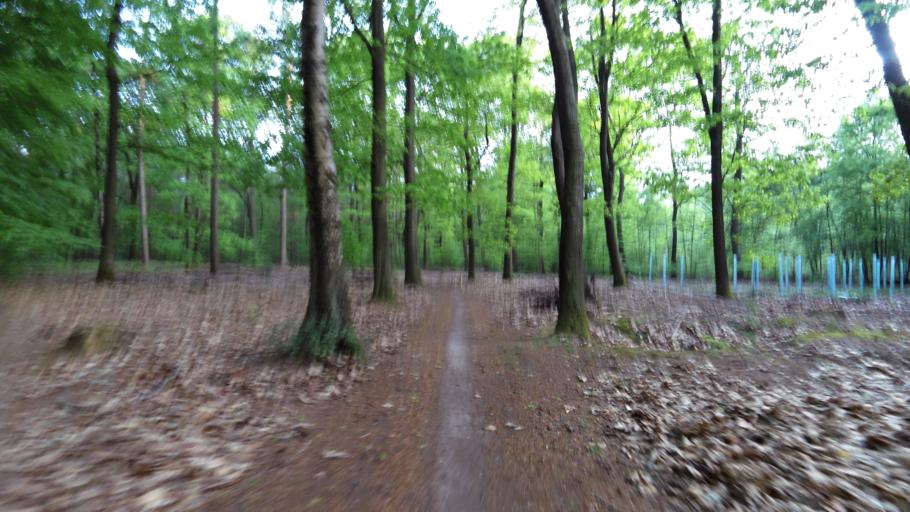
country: NL
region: Gelderland
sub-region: Gemeente Ede
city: Ede
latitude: 52.0484
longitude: 5.6876
